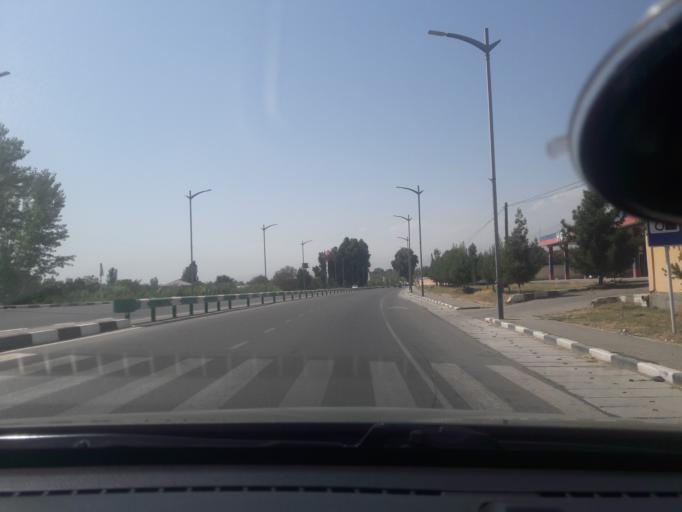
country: TJ
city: Shahrinav
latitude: 38.5629
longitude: 68.4161
